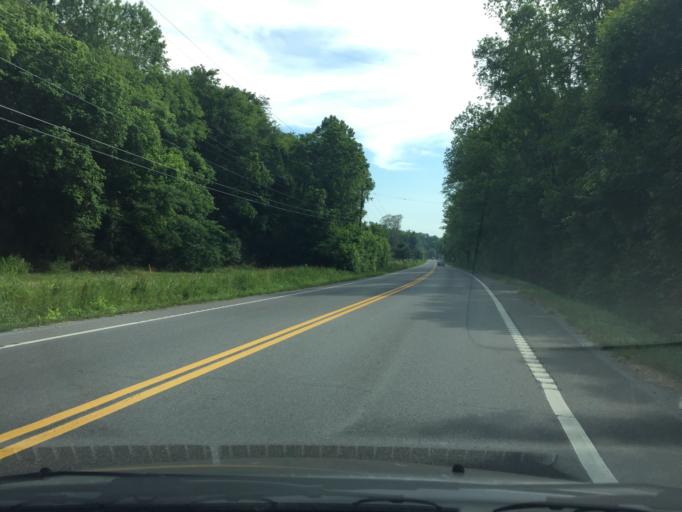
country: US
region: Tennessee
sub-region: Hamilton County
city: Collegedale
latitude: 35.0793
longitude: -85.0339
